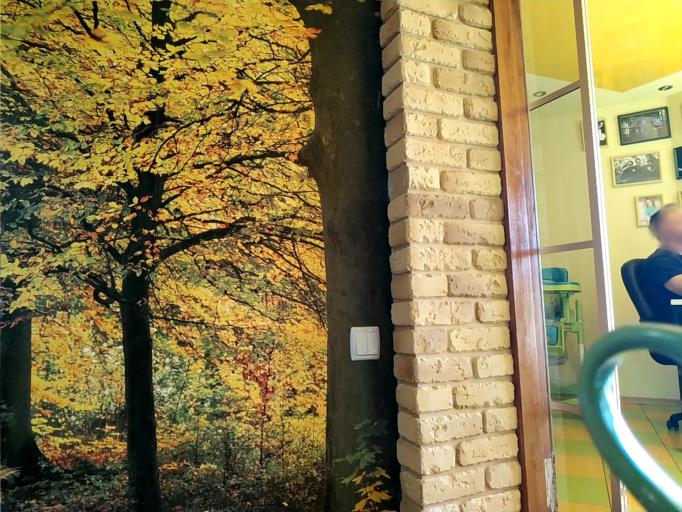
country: RU
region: Moskovskaya
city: Krasnoarmeysk
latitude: 56.0713
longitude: 38.2083
